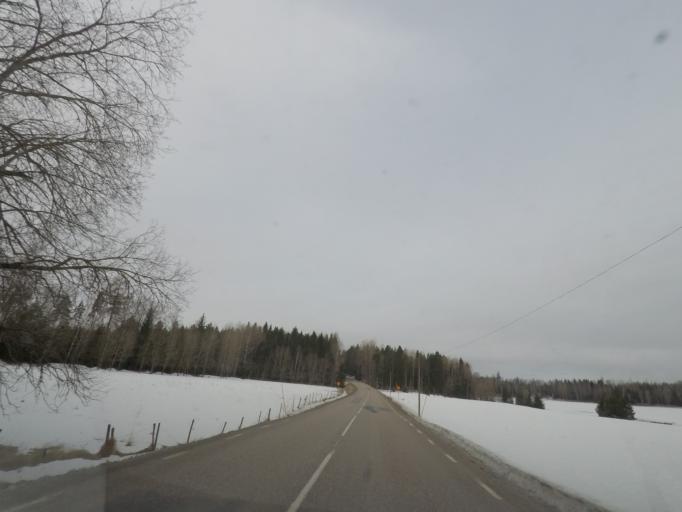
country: SE
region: Vaestmanland
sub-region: Vasteras
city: Skultuna
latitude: 59.7474
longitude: 16.3485
